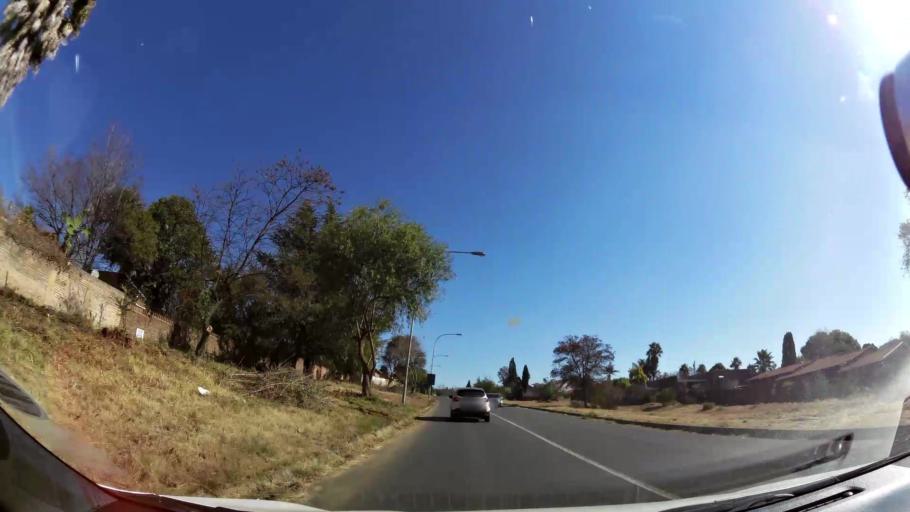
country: ZA
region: Gauteng
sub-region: City of Johannesburg Metropolitan Municipality
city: Johannesburg
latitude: -26.2873
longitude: 28.0617
